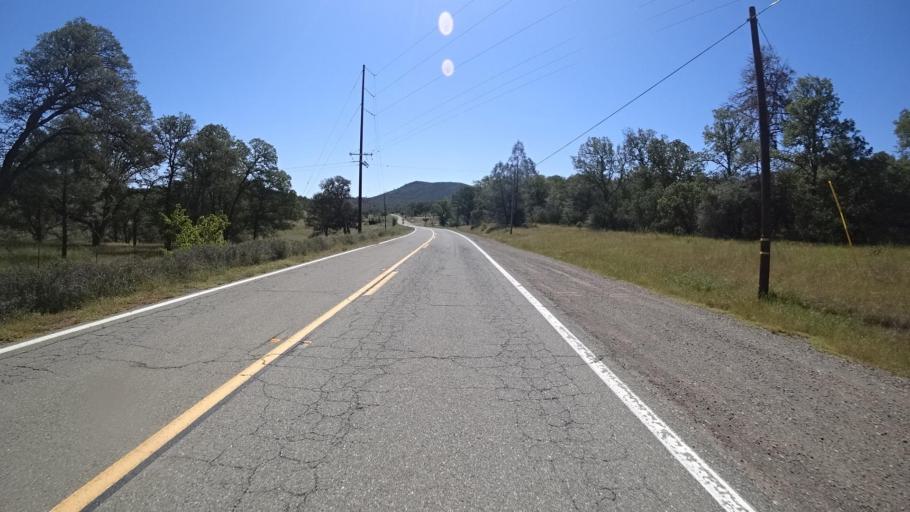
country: US
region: California
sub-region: Lake County
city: Hidden Valley Lake
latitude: 38.8874
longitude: -122.4797
